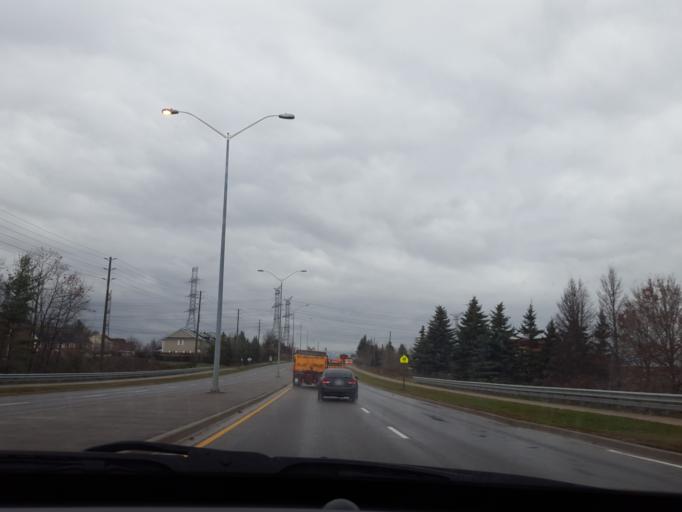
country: CA
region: Ontario
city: Ajax
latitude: 43.8632
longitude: -79.0811
